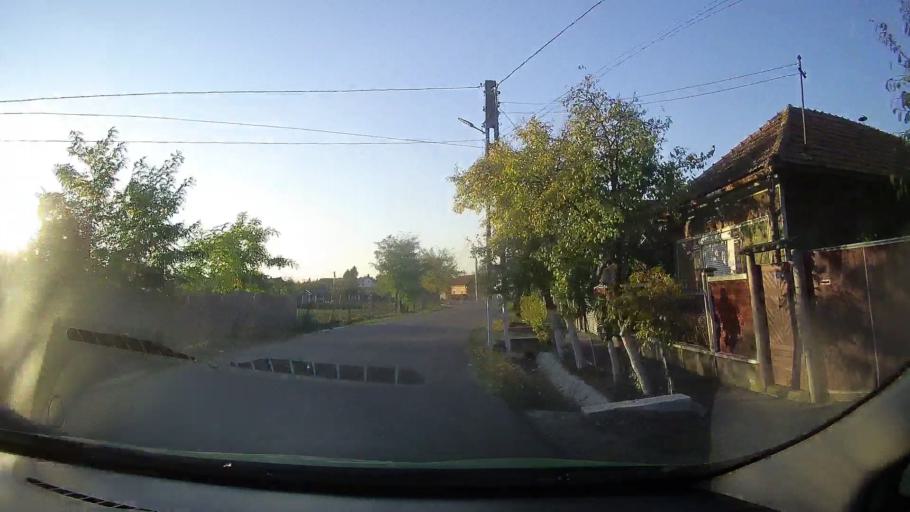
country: RO
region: Bihor
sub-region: Comuna Salard
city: Salard
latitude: 47.2234
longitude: 22.0332
